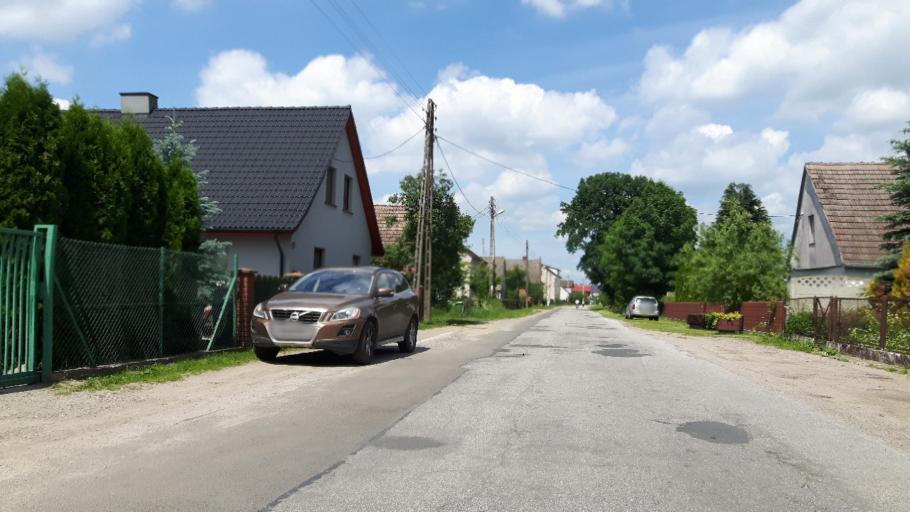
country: PL
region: West Pomeranian Voivodeship
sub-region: Powiat goleniowski
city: Osina
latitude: 53.6564
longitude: 14.9759
